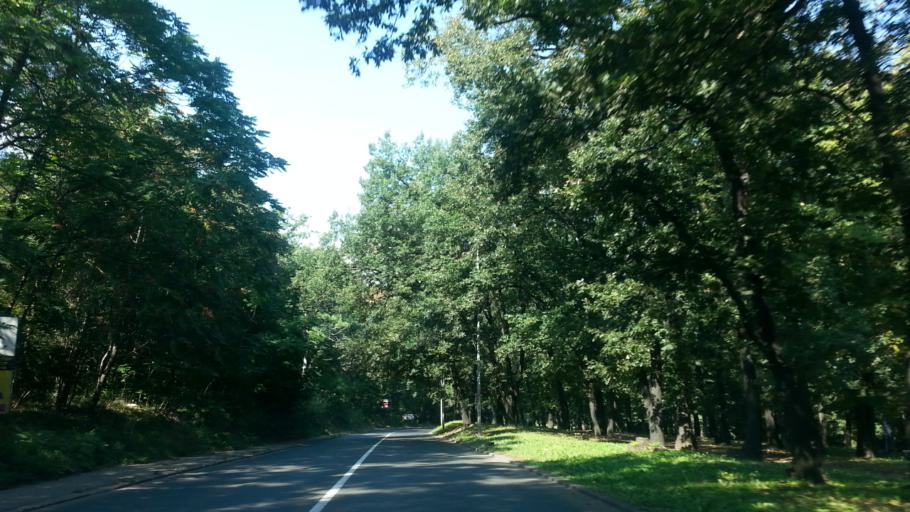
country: RS
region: Central Serbia
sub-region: Belgrade
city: Rakovica
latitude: 44.7608
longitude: 20.4313
